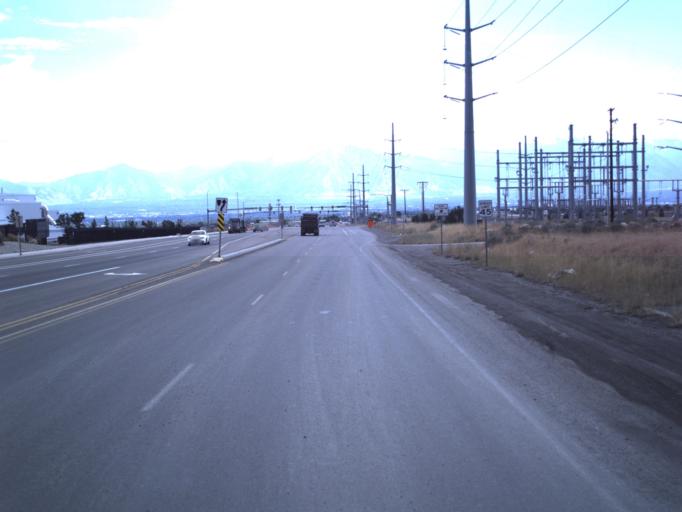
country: US
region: Utah
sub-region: Salt Lake County
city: Oquirrh
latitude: 40.6530
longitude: -112.0485
